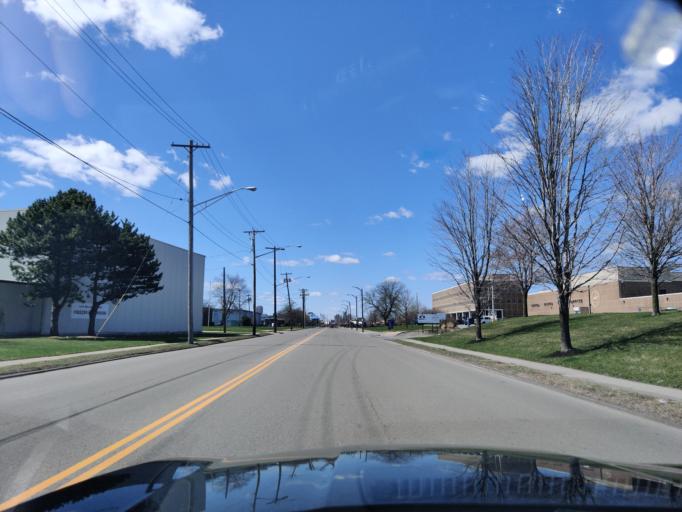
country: US
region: New York
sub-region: Erie County
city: Sloan
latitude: 42.8849
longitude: -78.8247
